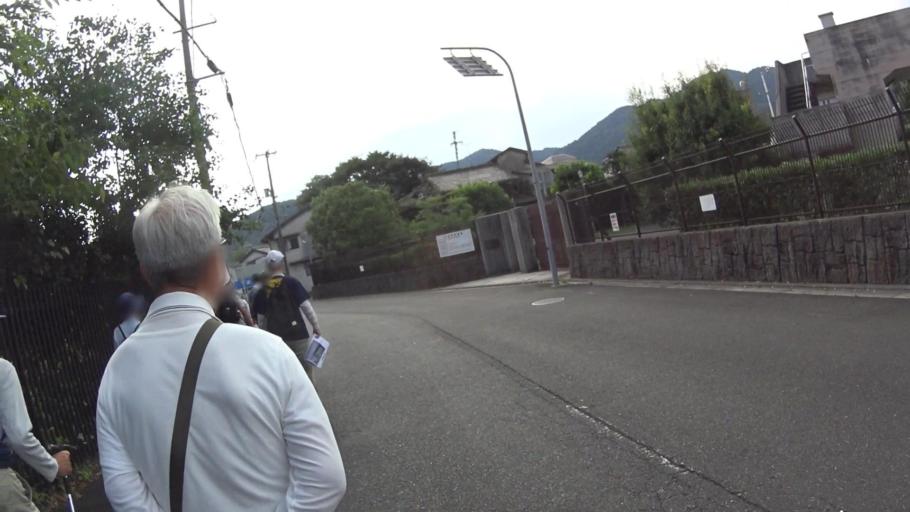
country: JP
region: Osaka
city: Kishiwada
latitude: 34.5015
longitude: 135.3341
